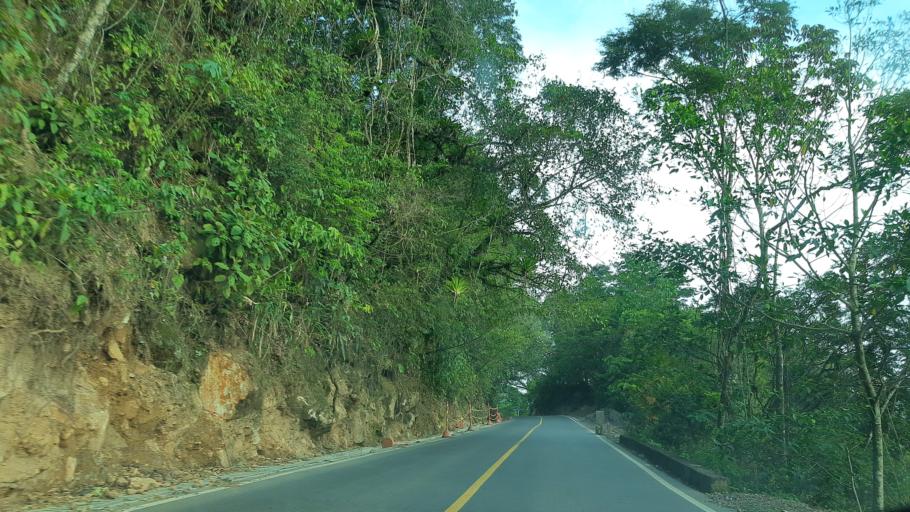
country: CO
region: Boyaca
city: San Luis de Gaceno
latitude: 4.8291
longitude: -73.2053
